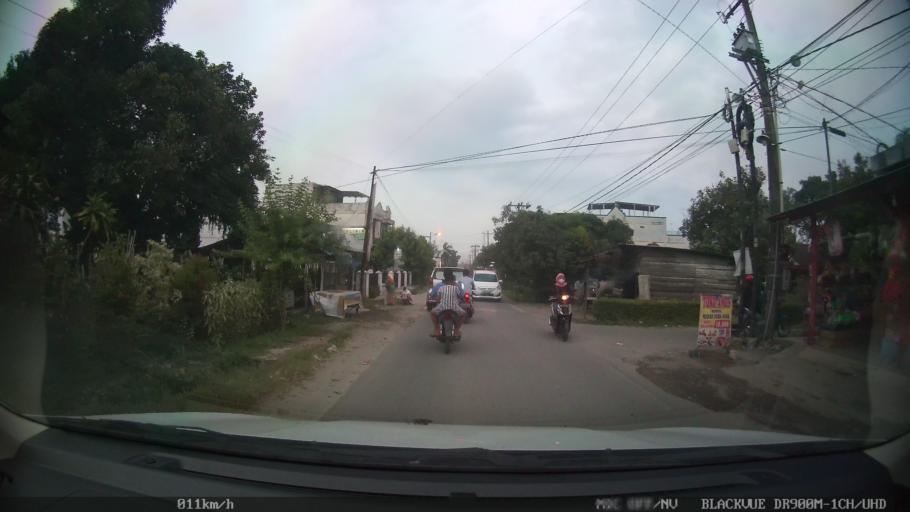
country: ID
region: North Sumatra
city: Sunggal
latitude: 3.5856
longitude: 98.5944
